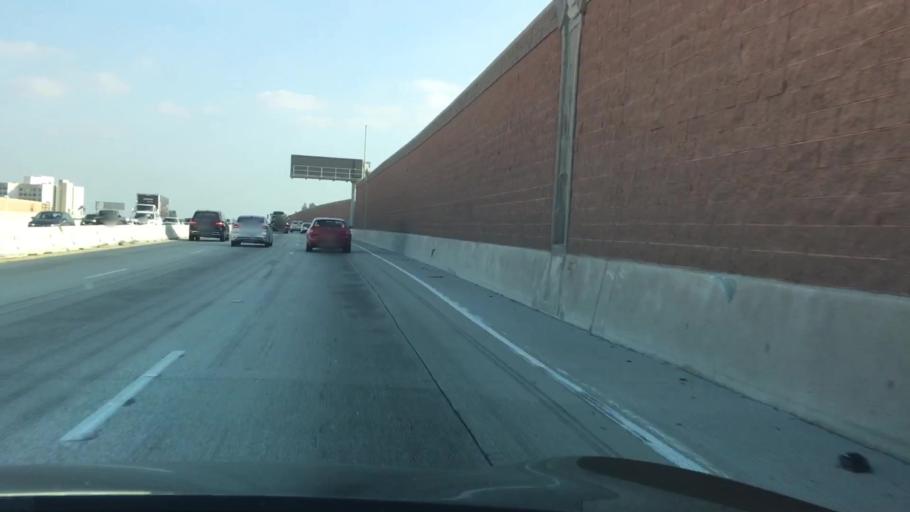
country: US
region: California
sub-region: Los Angeles County
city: Norwalk
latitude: 33.9143
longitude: -118.0775
